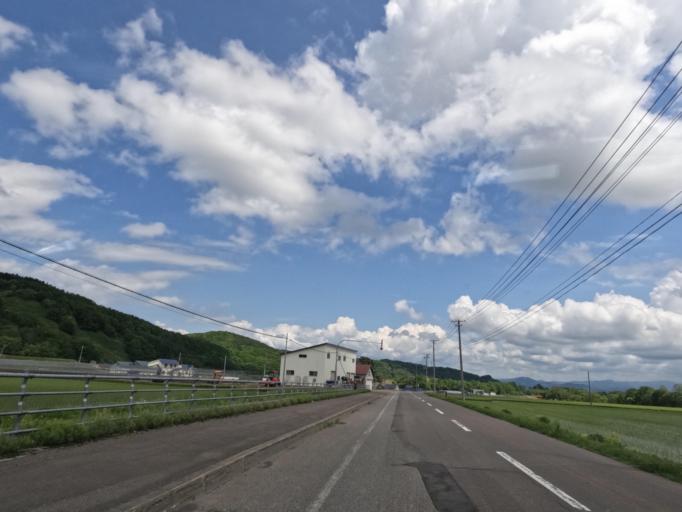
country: JP
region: Hokkaido
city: Takikawa
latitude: 43.5829
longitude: 141.8085
